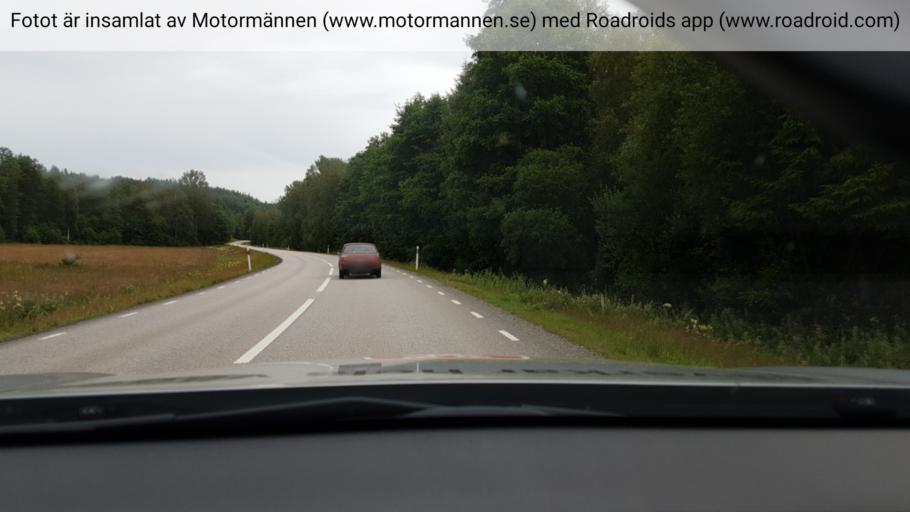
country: SE
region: Vaestra Goetaland
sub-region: Bengtsfors Kommun
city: Dals Langed
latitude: 58.8837
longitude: 12.2109
